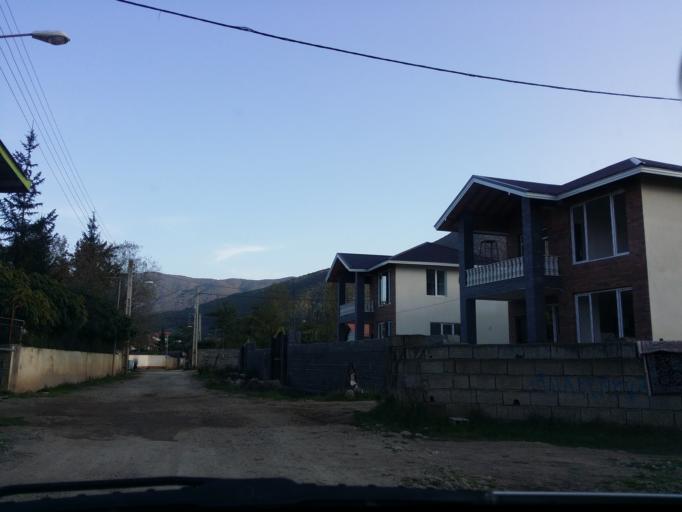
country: IR
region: Mazandaran
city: `Abbasabad
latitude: 36.5120
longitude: 51.1829
